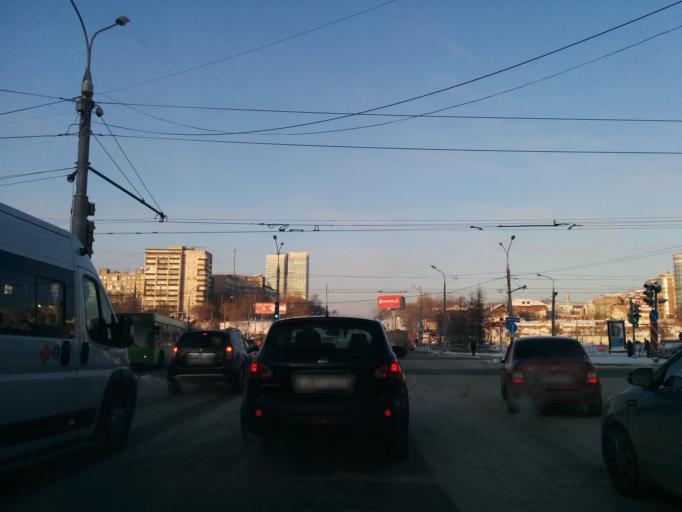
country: RU
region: Perm
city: Perm
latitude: 58.0089
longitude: 56.2274
